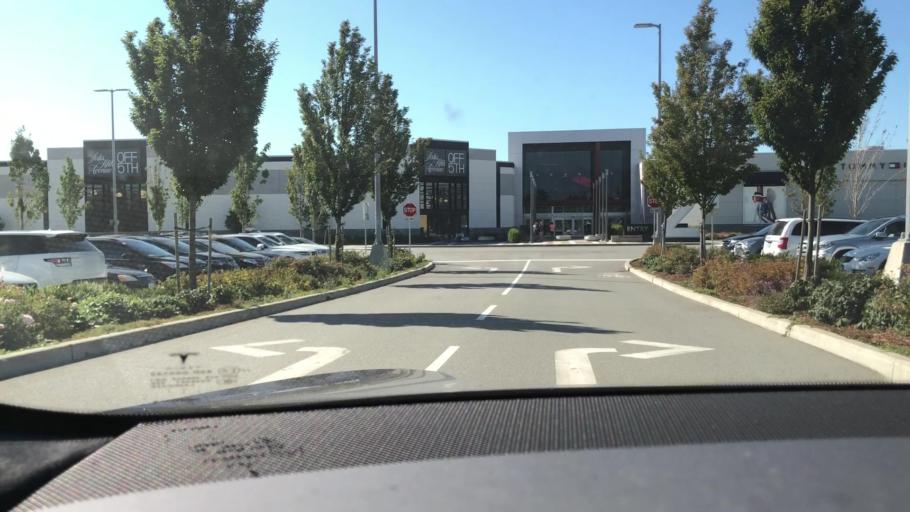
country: US
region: Washington
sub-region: Whatcom County
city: Point Roberts
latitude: 49.0365
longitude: -123.0850
